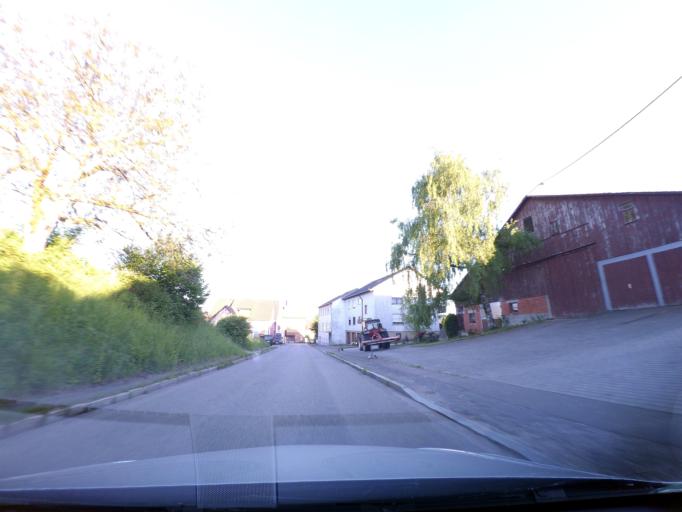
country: DE
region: Baden-Wuerttemberg
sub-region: Regierungsbezirk Stuttgart
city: Murrhardt
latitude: 48.9558
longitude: 9.5820
